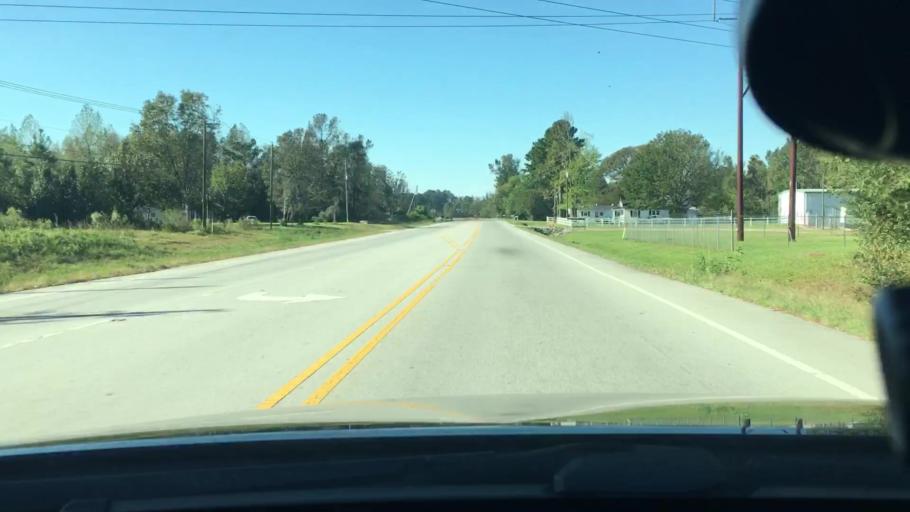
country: US
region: North Carolina
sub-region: Craven County
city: Trent Woods
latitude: 35.1558
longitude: -77.1130
